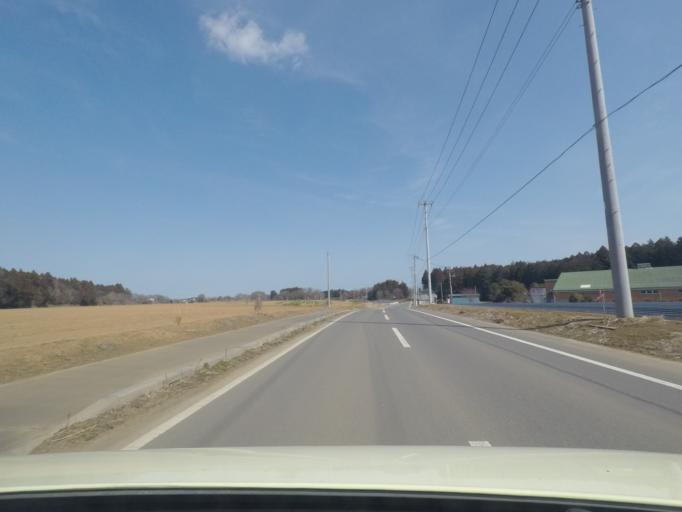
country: JP
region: Ibaraki
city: Okunoya
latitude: 36.1835
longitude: 140.3847
